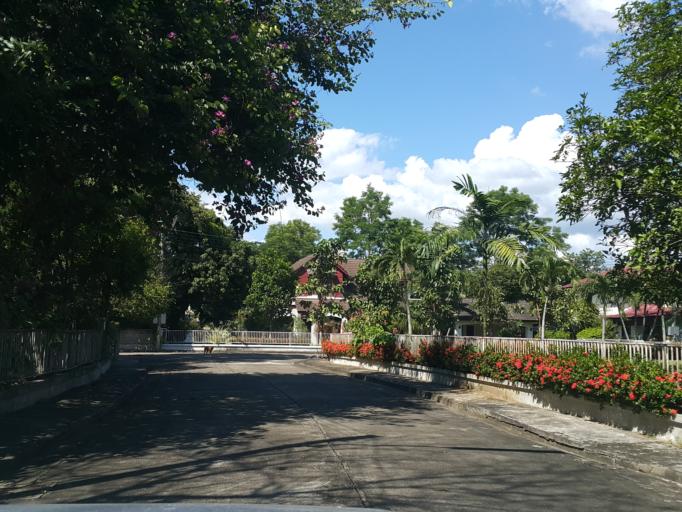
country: TH
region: Chiang Mai
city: San Sai
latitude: 18.8500
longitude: 99.0058
